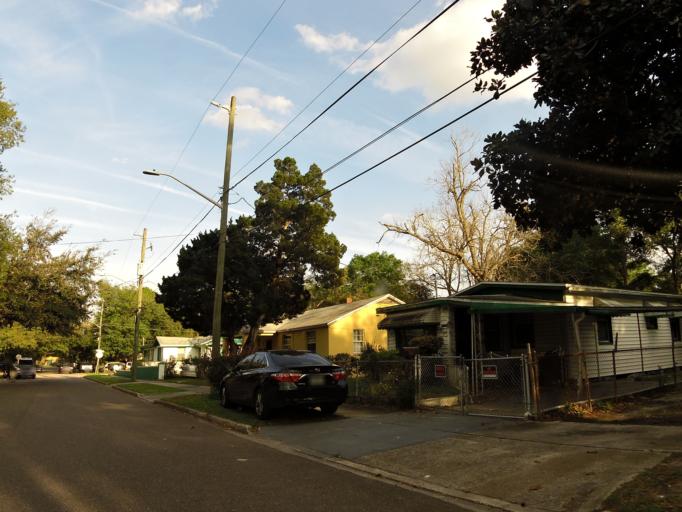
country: US
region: Florida
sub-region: Duval County
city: Jacksonville
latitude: 30.3496
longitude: -81.6841
